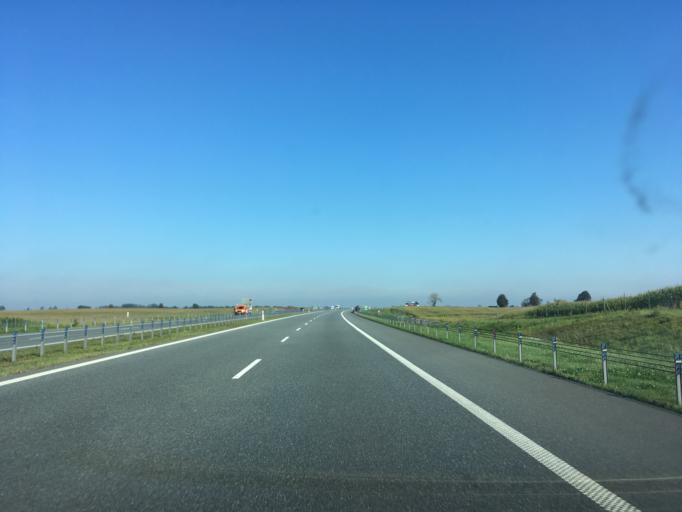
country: PL
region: Kujawsko-Pomorskie
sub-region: Powiat wabrzeski
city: Pluznica
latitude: 53.1863
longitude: 18.7375
